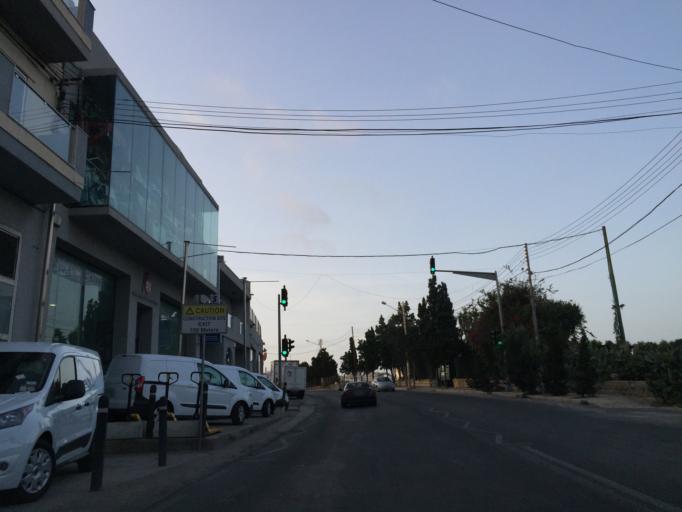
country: MT
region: Saint Paul's Bay
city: San Pawl il-Bahar
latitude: 35.9397
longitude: 14.4114
